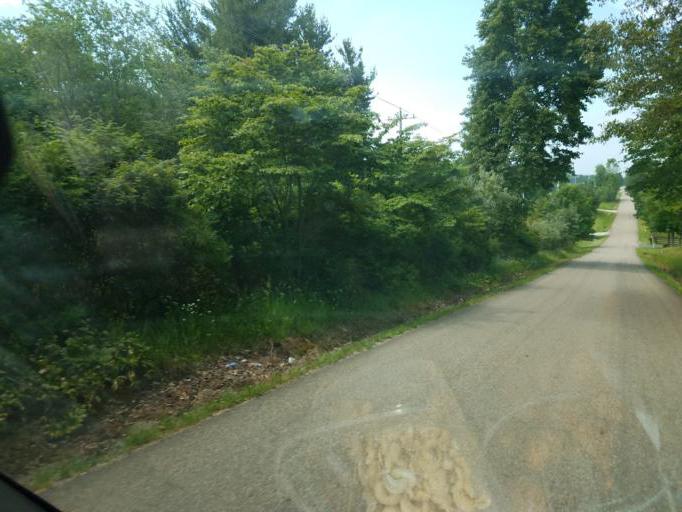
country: US
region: Ohio
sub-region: Knox County
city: Oak Hill
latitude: 40.2823
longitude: -82.2427
